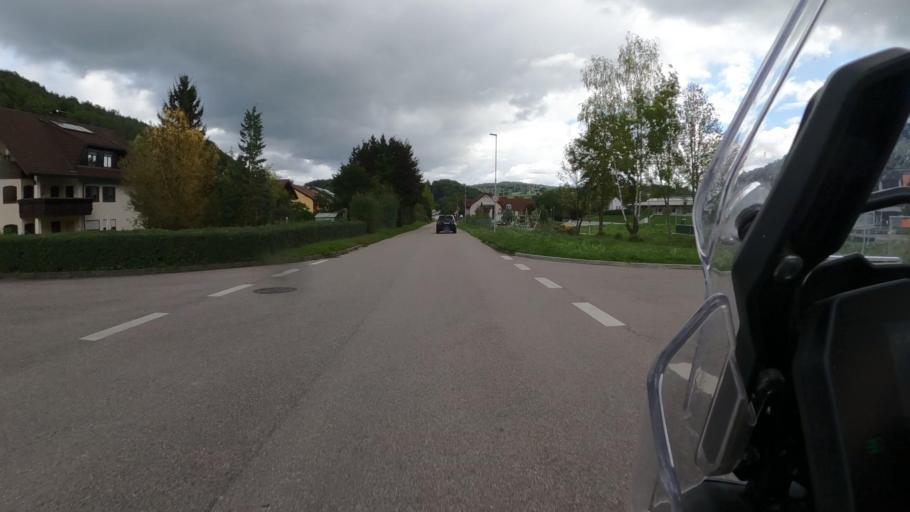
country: DE
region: Baden-Wuerttemberg
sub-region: Freiburg Region
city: Eggingen
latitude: 47.6991
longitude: 8.3899
